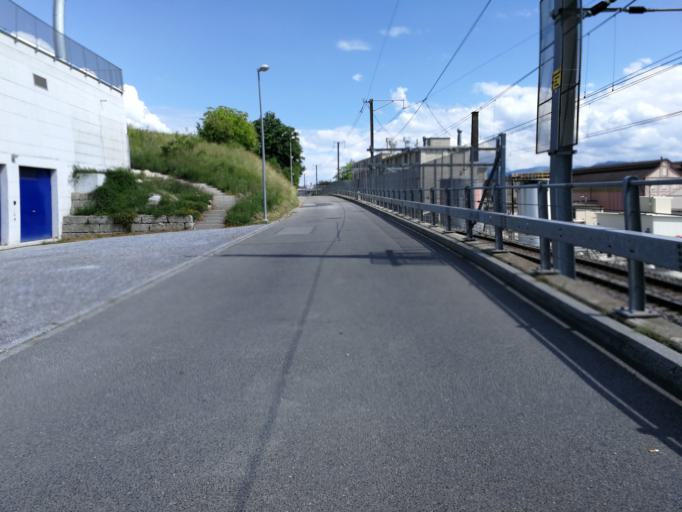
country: CH
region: Zurich
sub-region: Bezirk Meilen
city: Uetikon
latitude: 47.2609
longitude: 8.6726
